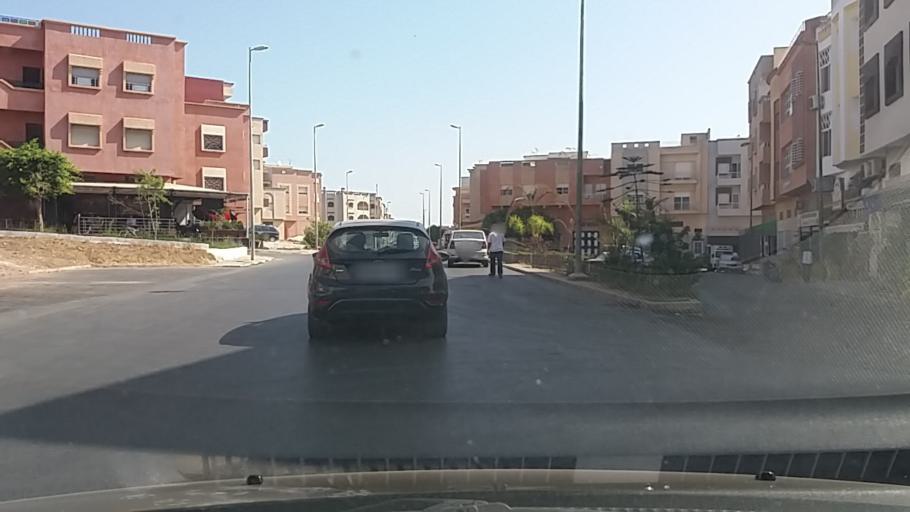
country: MA
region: Gharb-Chrarda-Beni Hssen
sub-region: Kenitra Province
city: Kenitra
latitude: 34.2703
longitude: -6.6105
